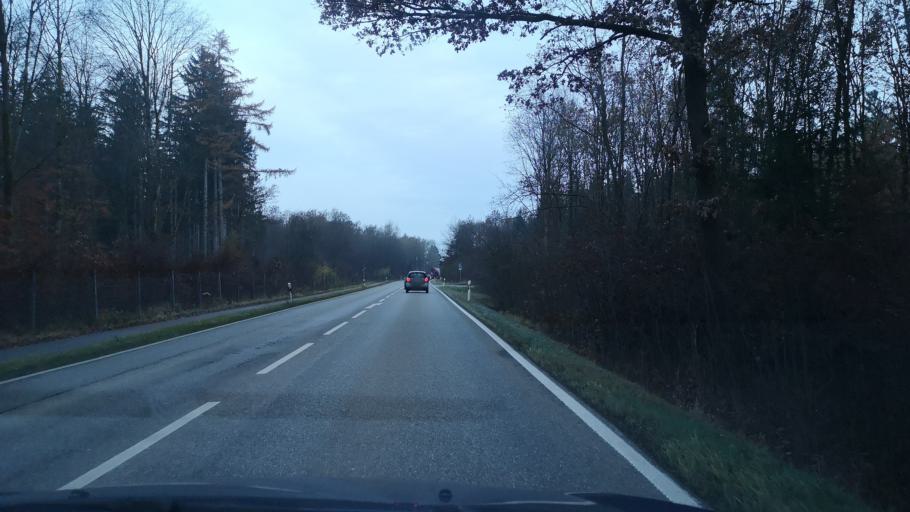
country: DE
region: Bavaria
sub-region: Upper Bavaria
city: Forstinning
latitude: 48.1539
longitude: 11.9080
